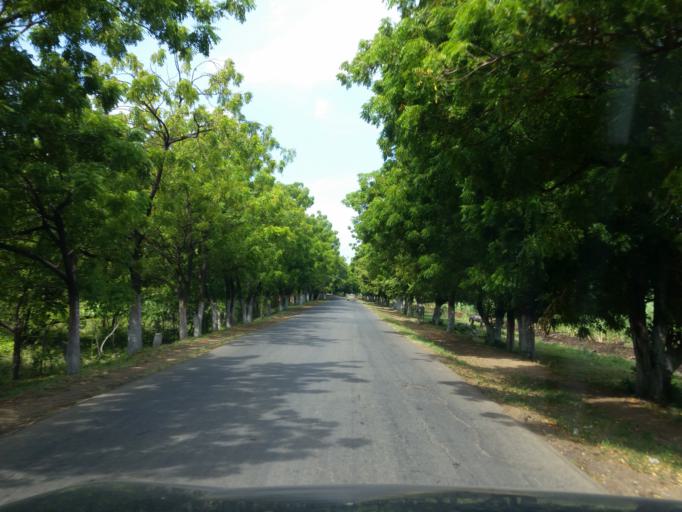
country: NI
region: Managua
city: Masachapa
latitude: 11.8078
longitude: -86.4936
